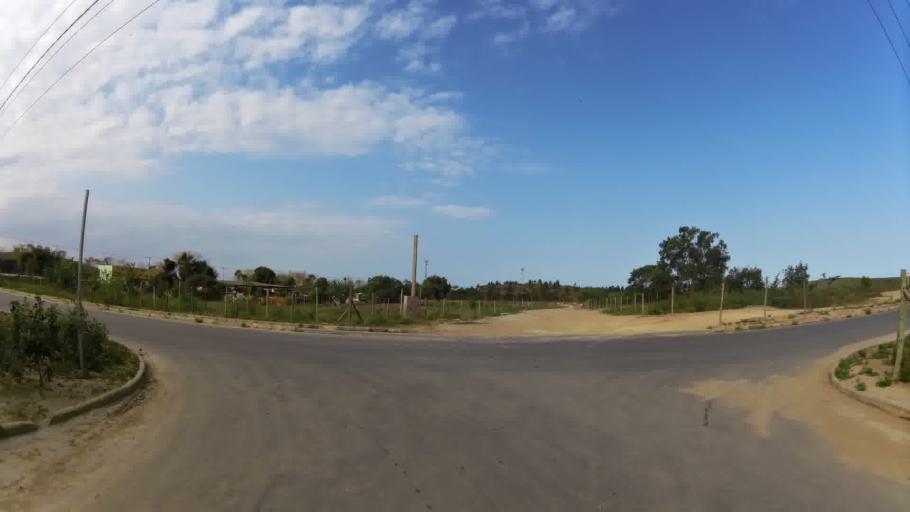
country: BR
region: Espirito Santo
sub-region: Itapemirim
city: Itapemirim
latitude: -21.0106
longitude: -40.8272
